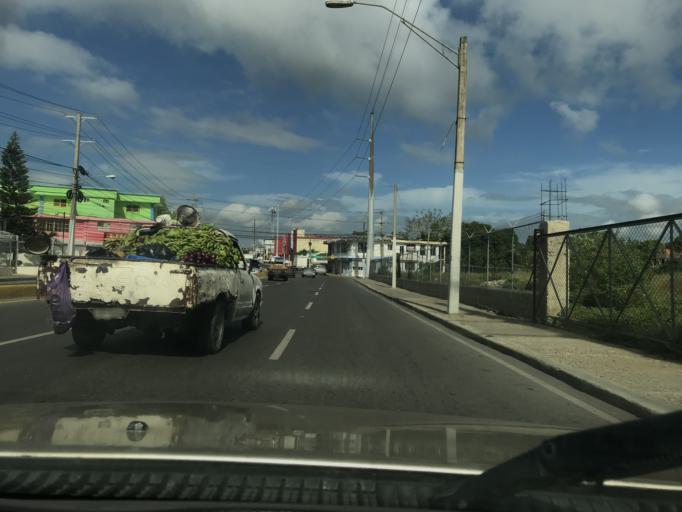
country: DO
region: Santiago
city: Santiago de los Caballeros
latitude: 19.4856
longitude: -70.7334
